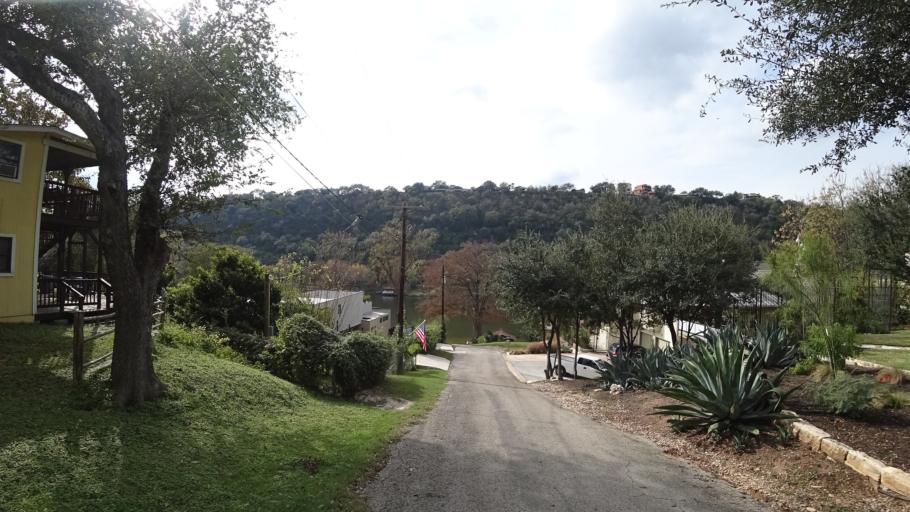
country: US
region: Texas
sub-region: Travis County
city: Hudson Bend
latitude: 30.3833
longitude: -97.9131
